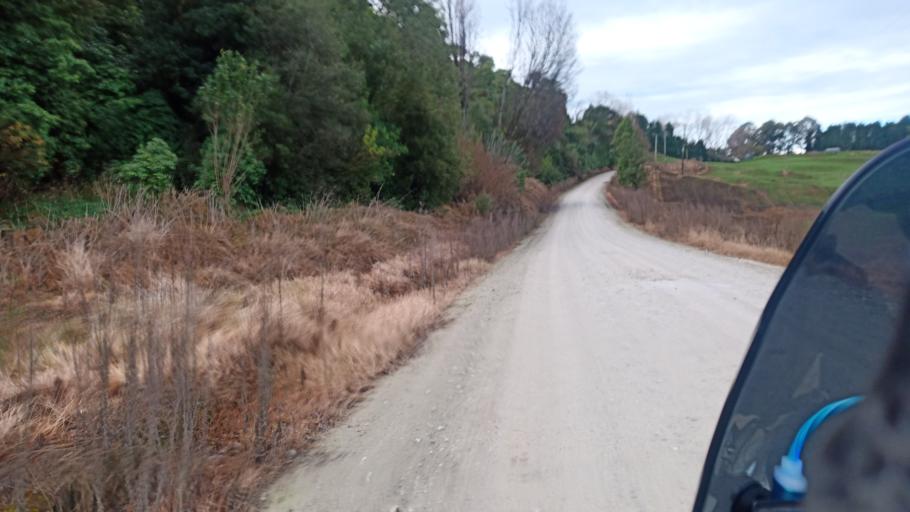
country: NZ
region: Gisborne
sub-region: Gisborne District
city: Gisborne
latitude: -38.3819
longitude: 177.9603
